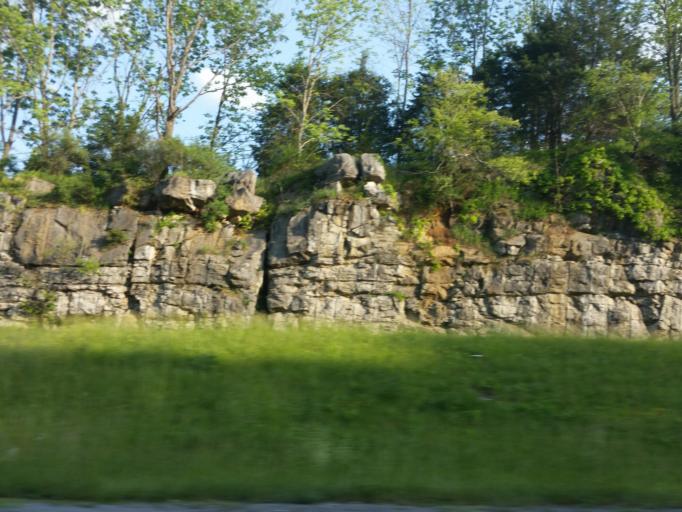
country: US
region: Virginia
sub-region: Tazewell County
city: Claypool Hill
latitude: 37.0694
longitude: -81.7262
